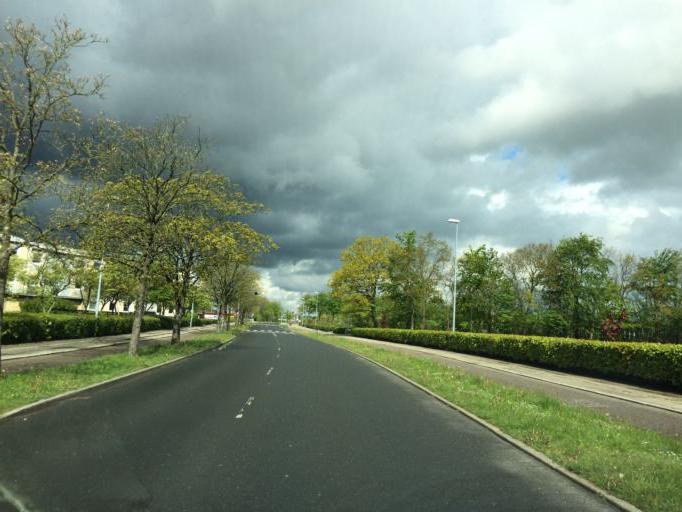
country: DK
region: Central Jutland
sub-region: Holstebro Kommune
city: Holstebro
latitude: 56.3673
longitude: 8.6072
